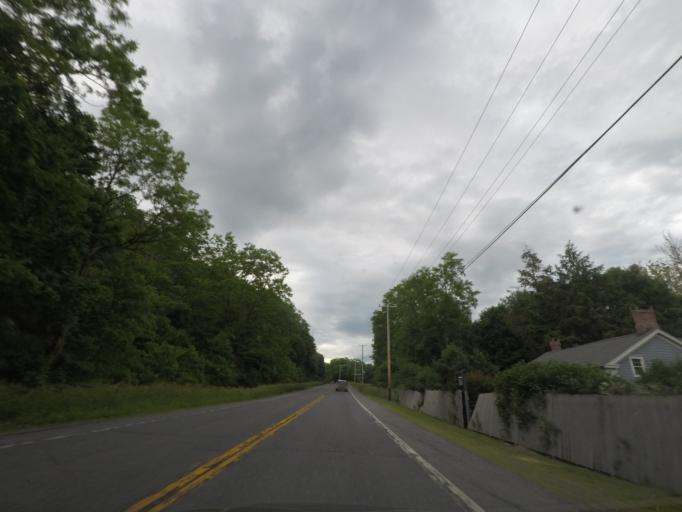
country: US
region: New York
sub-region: Dutchess County
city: Pine Plains
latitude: 41.9756
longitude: -73.6417
